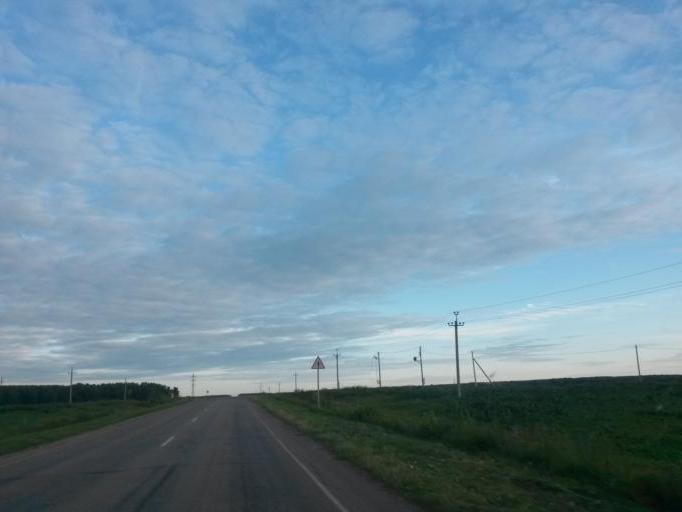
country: RU
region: Moskovskaya
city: Barybino
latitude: 55.2043
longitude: 37.7891
